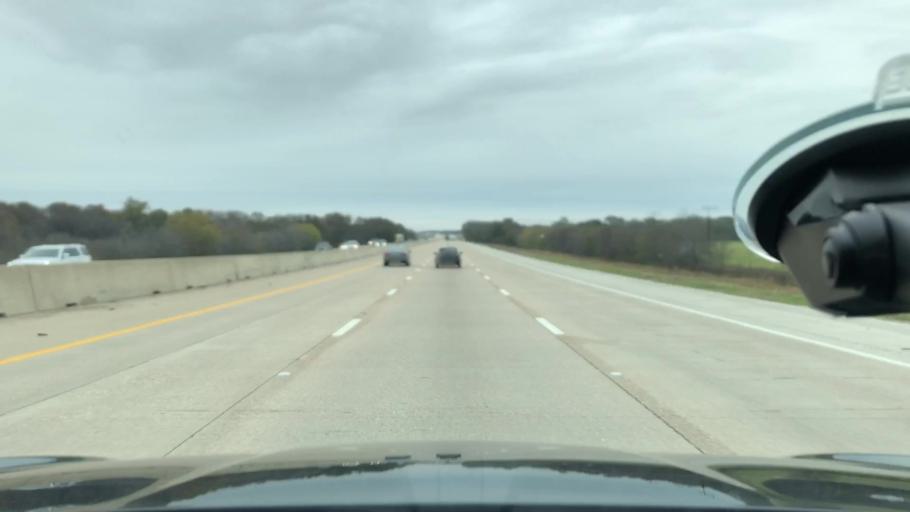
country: US
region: Texas
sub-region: Ellis County
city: Italy
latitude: 32.2244
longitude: -96.8855
